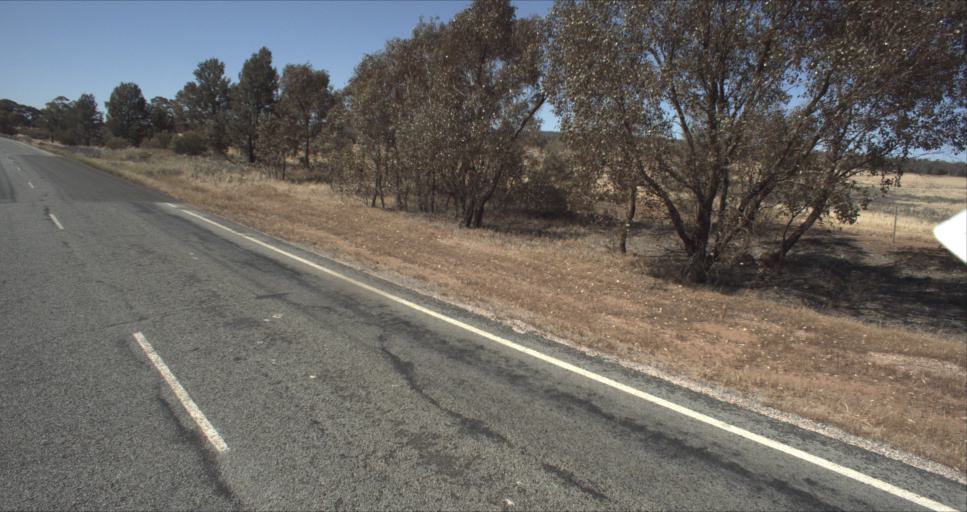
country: AU
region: New South Wales
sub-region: Leeton
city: Leeton
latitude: -34.4729
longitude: 146.4357
